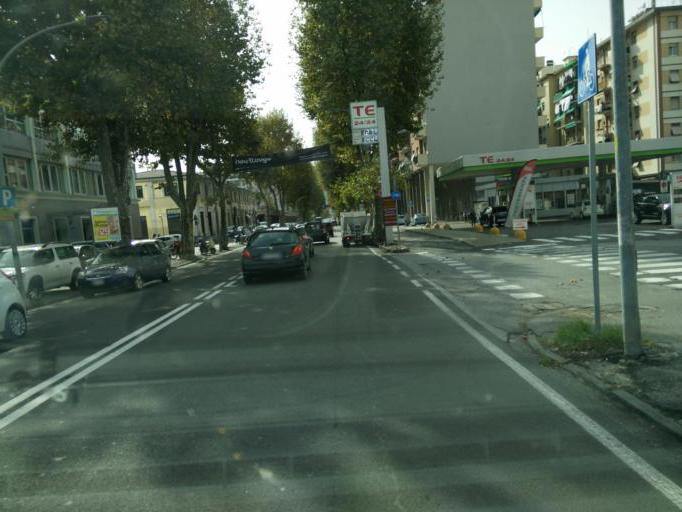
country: IT
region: Liguria
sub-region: Provincia di La Spezia
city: La Spezia
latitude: 44.1135
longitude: 9.8376
